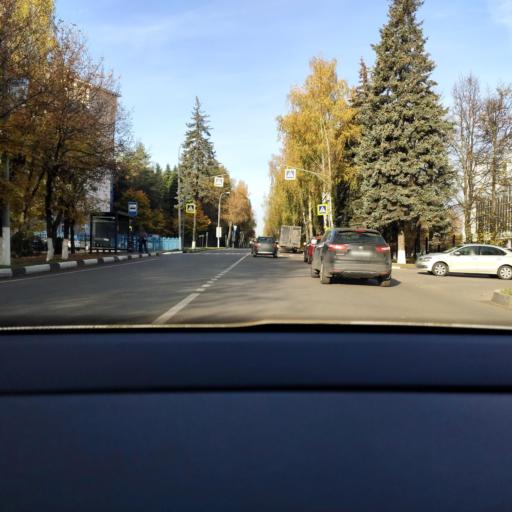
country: RU
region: Moskovskaya
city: Ivanteyevka
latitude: 55.9782
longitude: 37.9008
